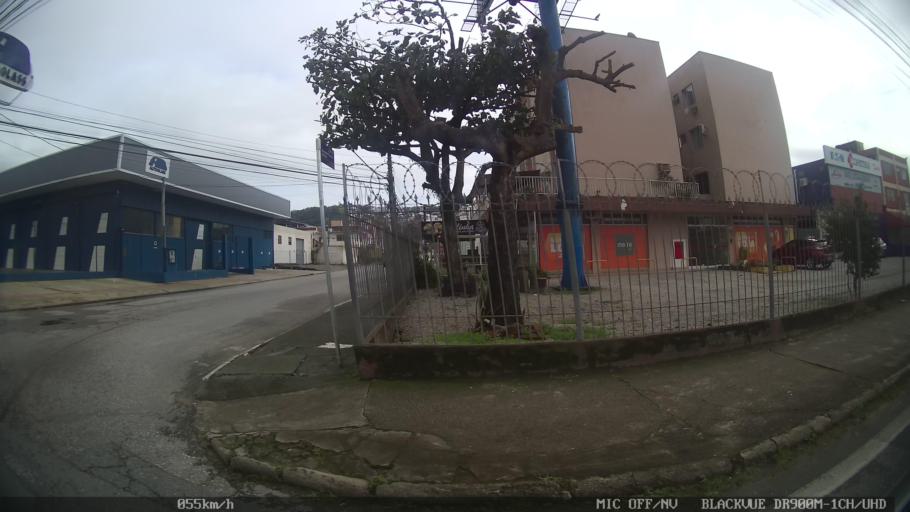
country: BR
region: Santa Catarina
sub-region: Sao Jose
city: Campinas
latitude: -27.5895
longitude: -48.6177
